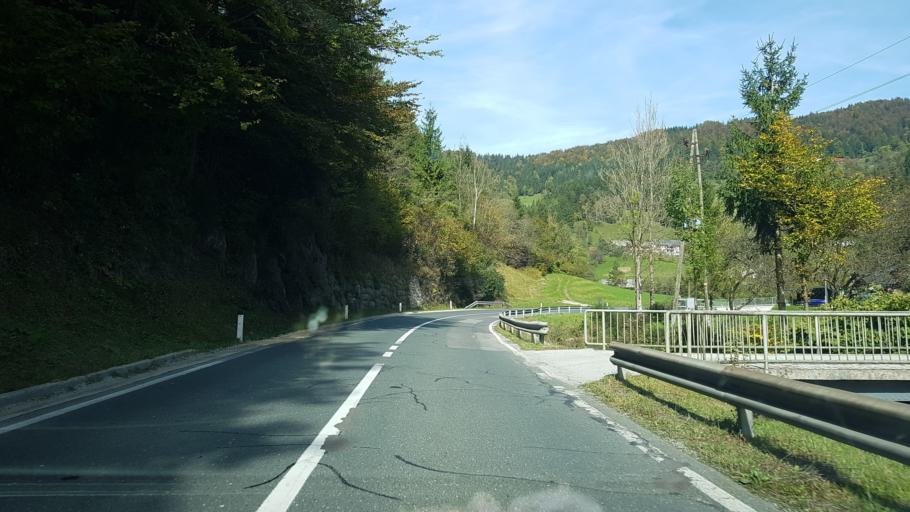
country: SI
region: Velenje
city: Velenje
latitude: 46.4067
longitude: 15.1790
